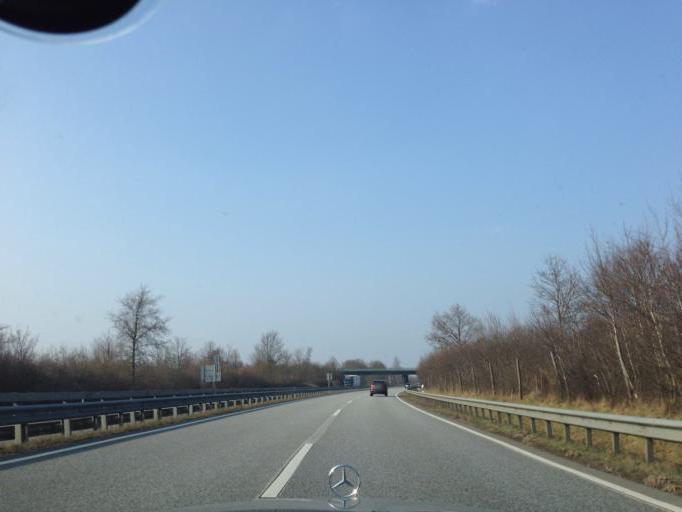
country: DE
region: Schleswig-Holstein
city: Negernbotel
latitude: 53.9718
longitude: 10.2413
